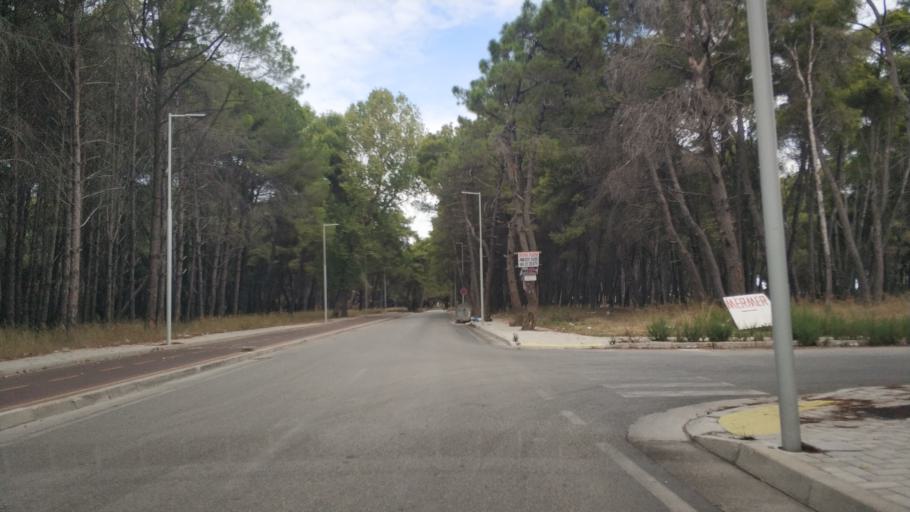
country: AL
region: Vlore
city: Vlore
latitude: 40.4663
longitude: 19.4619
